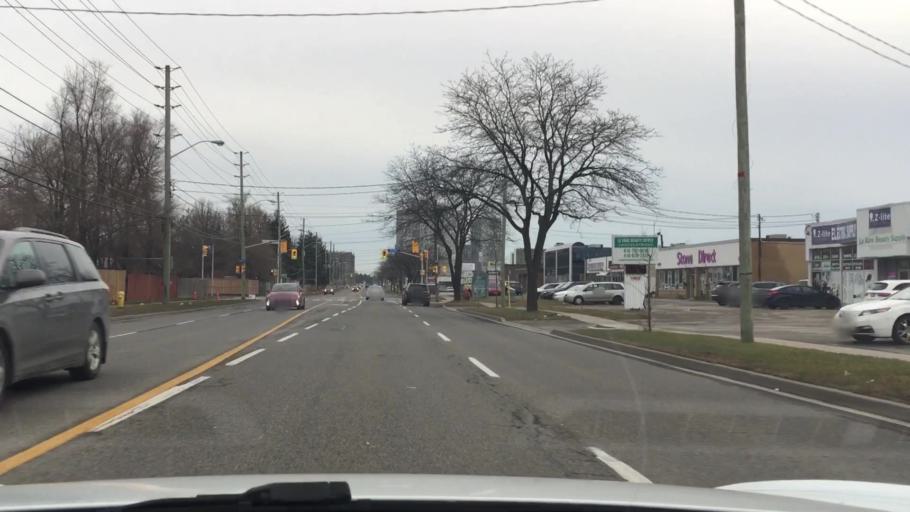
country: CA
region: Ontario
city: Scarborough
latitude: 43.7588
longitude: -79.2678
